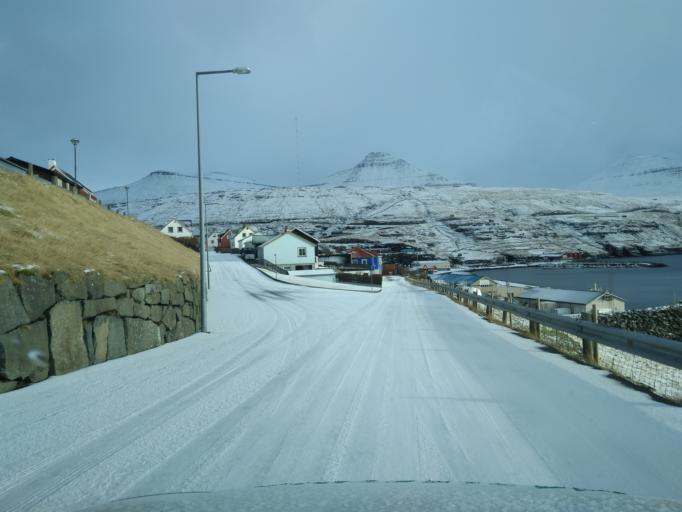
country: FO
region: Eysturoy
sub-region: Eidi
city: Eidi
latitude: 62.2987
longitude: -7.0993
